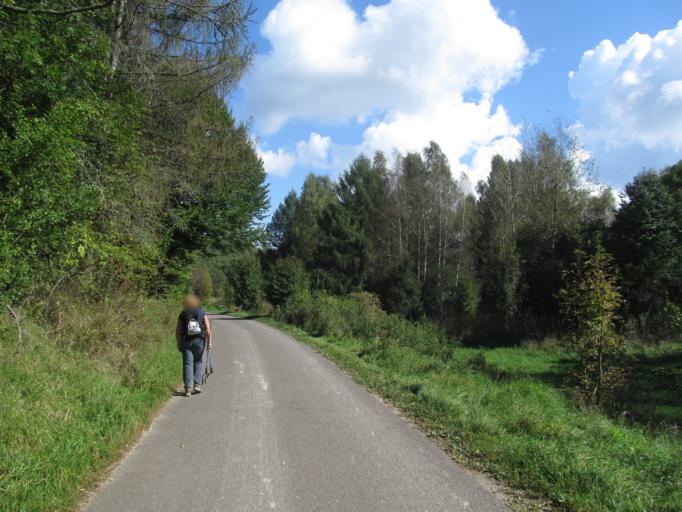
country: HU
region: Borsod-Abauj-Zemplen
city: Kazincbarcika
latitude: 48.1017
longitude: 20.5856
